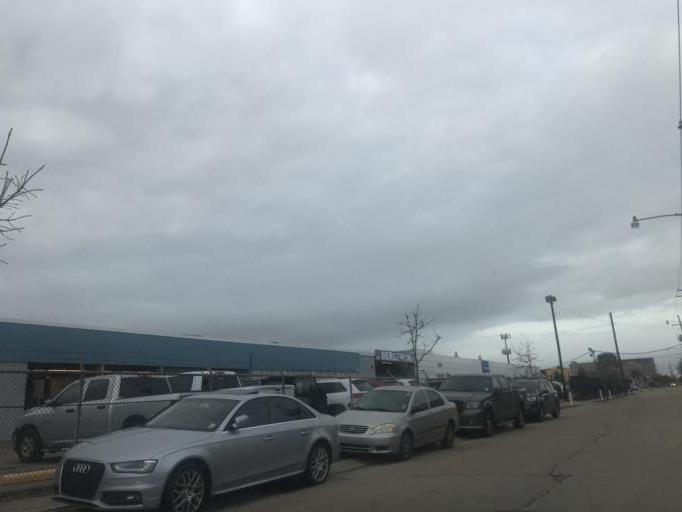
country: US
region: Louisiana
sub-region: Jefferson Parish
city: Metairie
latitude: 30.0046
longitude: -90.1606
